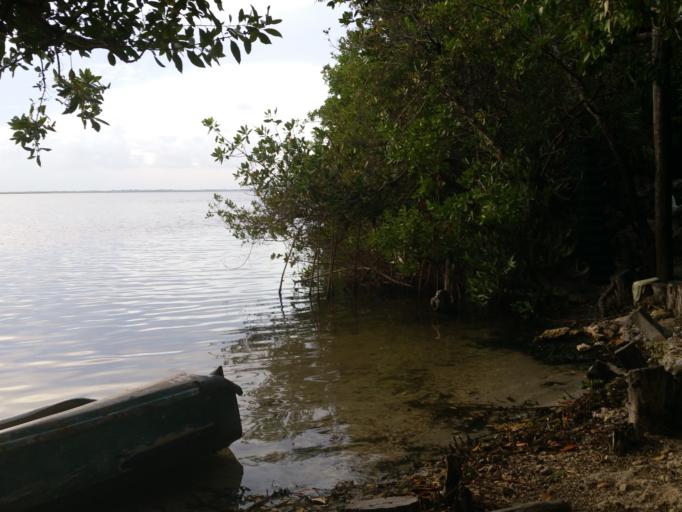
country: MX
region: Quintana Roo
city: Alfredo V. Bonfil
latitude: 21.0491
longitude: -86.7836
